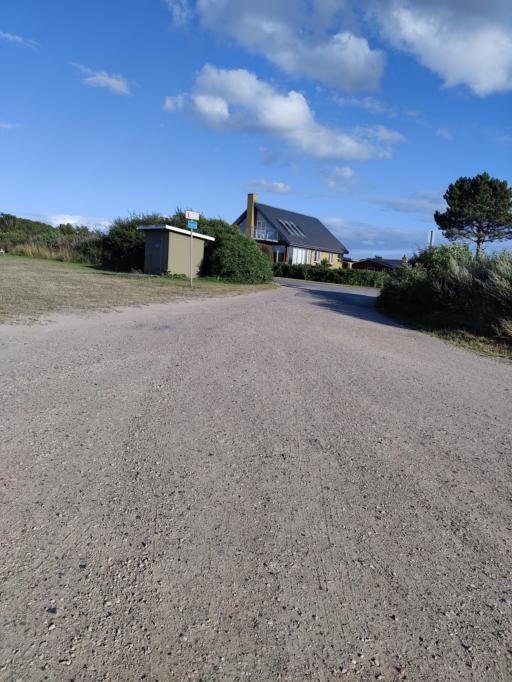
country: DK
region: South Denmark
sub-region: Assens Kommune
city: Assens
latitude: 55.3345
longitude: 9.8784
